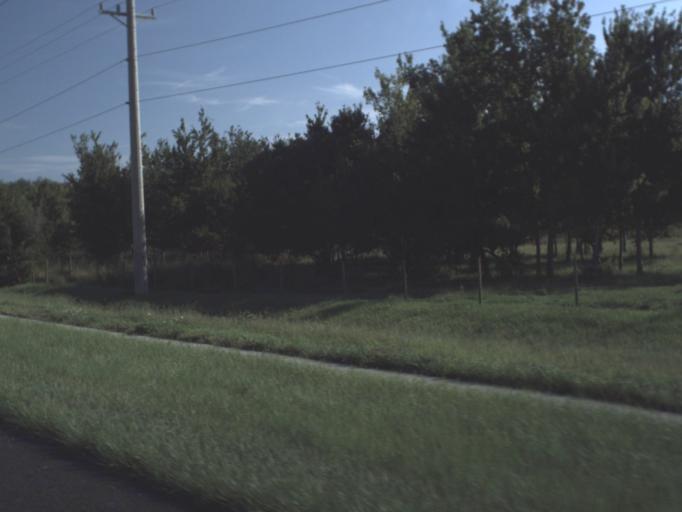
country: US
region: Florida
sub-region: Polk County
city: Gibsonia
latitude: 28.1322
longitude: -81.9735
